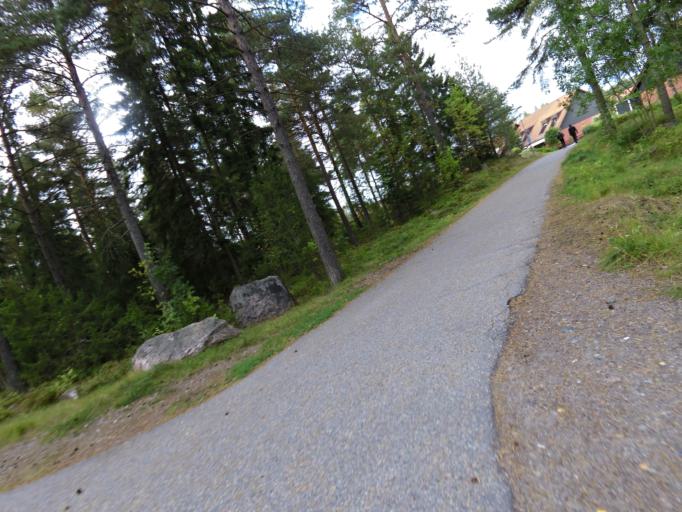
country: SE
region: Gaevleborg
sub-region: Gavle Kommun
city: Gavle
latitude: 60.6659
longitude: 17.2094
